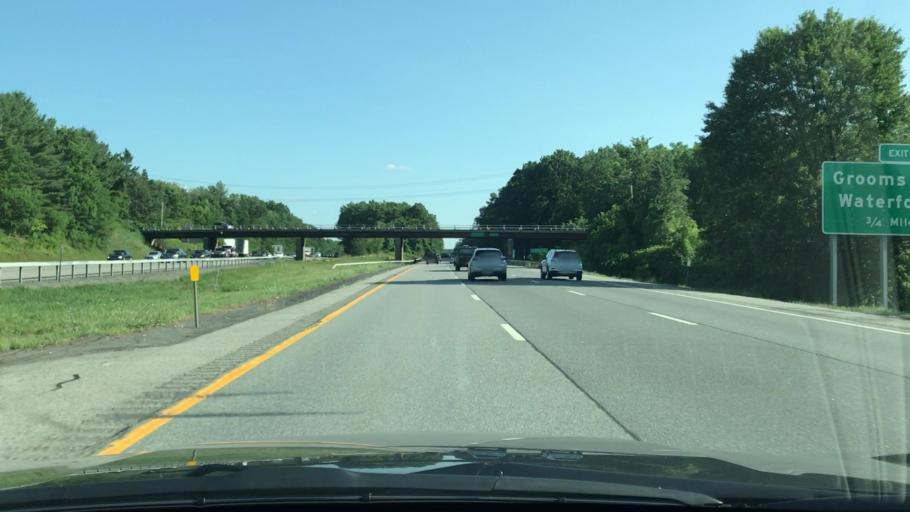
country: US
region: New York
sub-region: Saratoga County
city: Country Knolls
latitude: 42.8544
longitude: -73.7741
